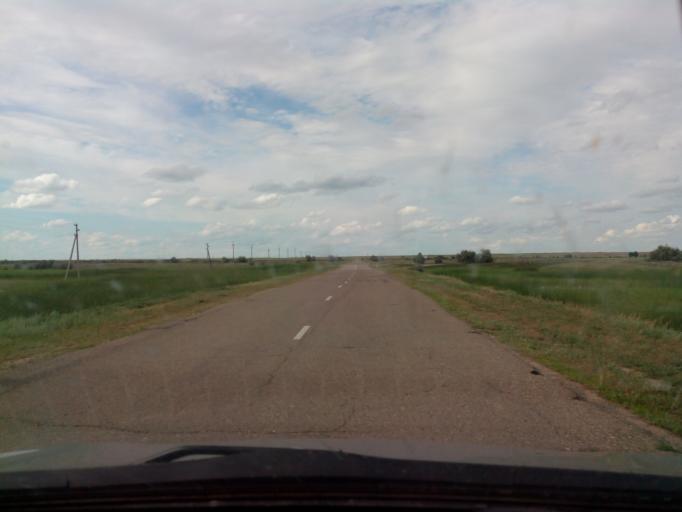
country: RU
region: Volgograd
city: Leninsk
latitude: 48.6760
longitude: 45.3695
